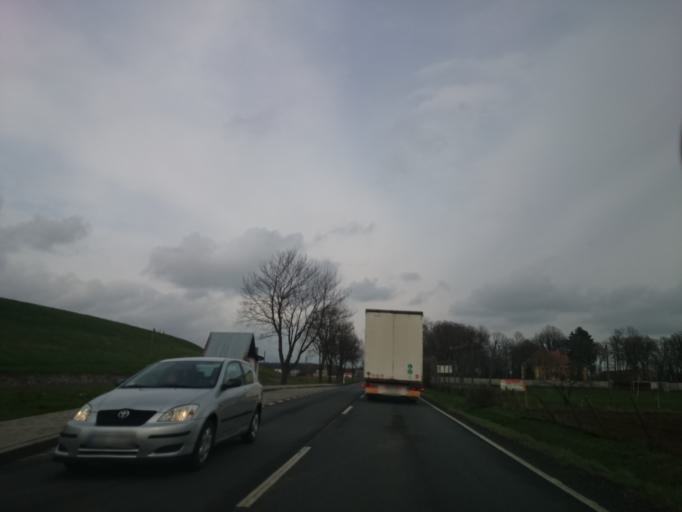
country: PL
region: Opole Voivodeship
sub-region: Powiat nyski
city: Otmuchow
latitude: 50.4509
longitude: 17.1428
